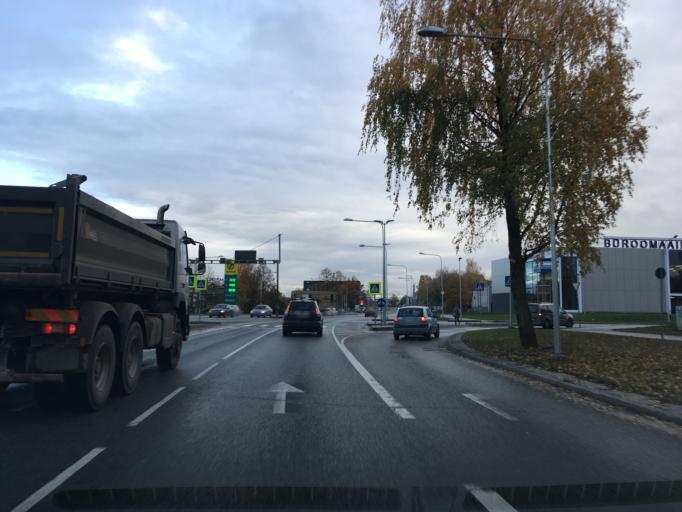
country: EE
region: Tartu
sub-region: Tartu linn
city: Tartu
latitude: 58.3695
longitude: 26.7413
